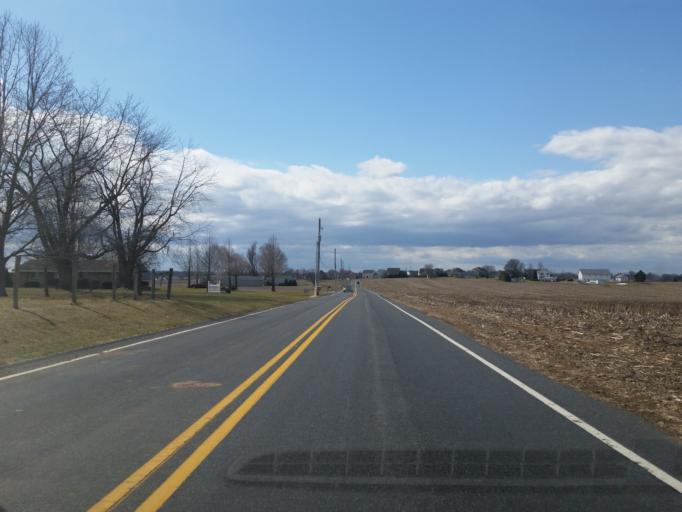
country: US
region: Pennsylvania
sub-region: Lebanon County
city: Palmyra
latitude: 40.3099
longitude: -76.5565
